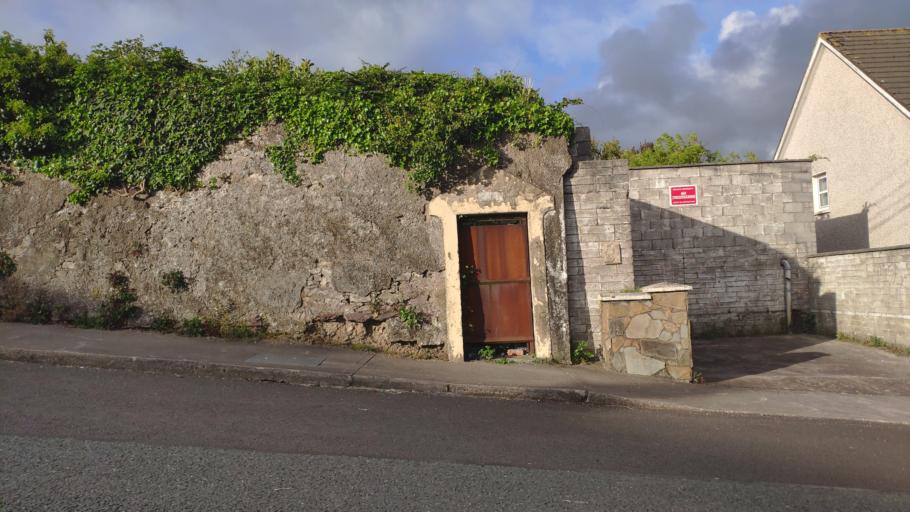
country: IE
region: Munster
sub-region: County Cork
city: Cork
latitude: 51.9089
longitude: -8.4842
